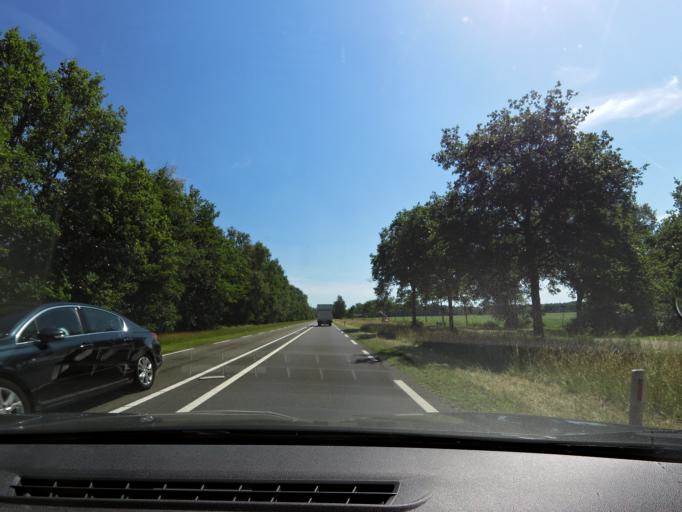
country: NL
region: Gelderland
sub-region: Oost Gelre
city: Lichtenvoorde
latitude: 52.0262
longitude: 6.6150
